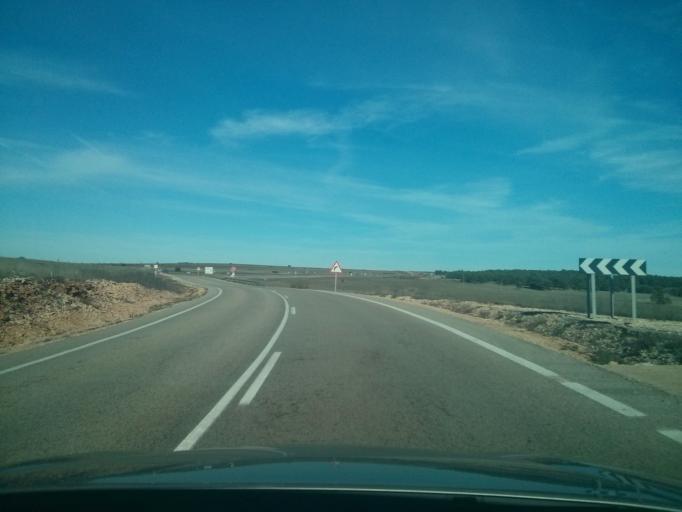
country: ES
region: Castille and Leon
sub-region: Provincia de Burgos
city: Abajas
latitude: 42.6482
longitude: -3.6258
